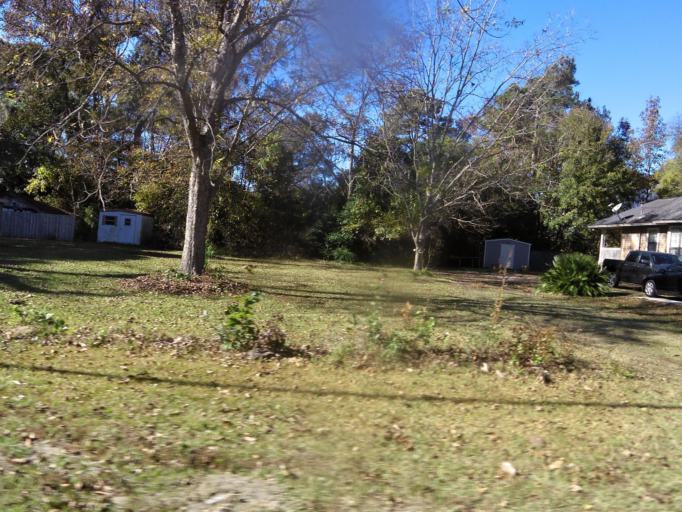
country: US
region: Georgia
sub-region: Chatham County
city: Garden City
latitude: 32.0899
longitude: -81.1583
